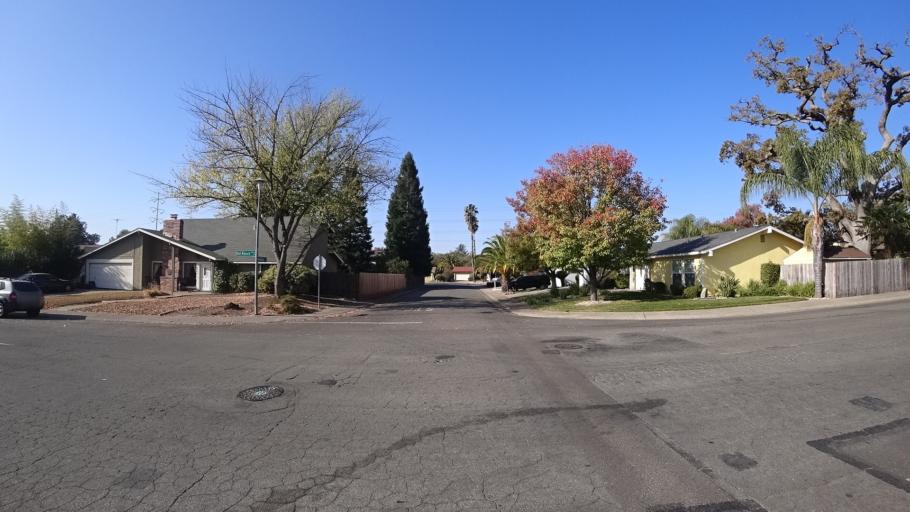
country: US
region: California
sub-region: Sacramento County
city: Citrus Heights
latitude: 38.6996
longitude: -121.2514
